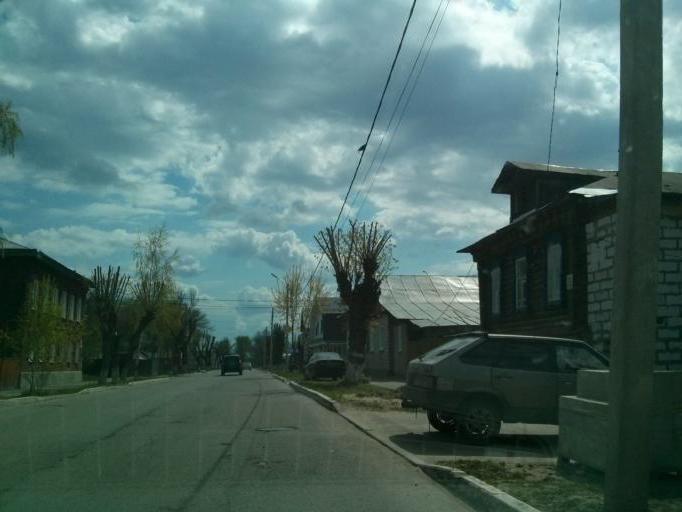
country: RU
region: Vladimir
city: Murom
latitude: 55.5694
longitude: 42.0643
